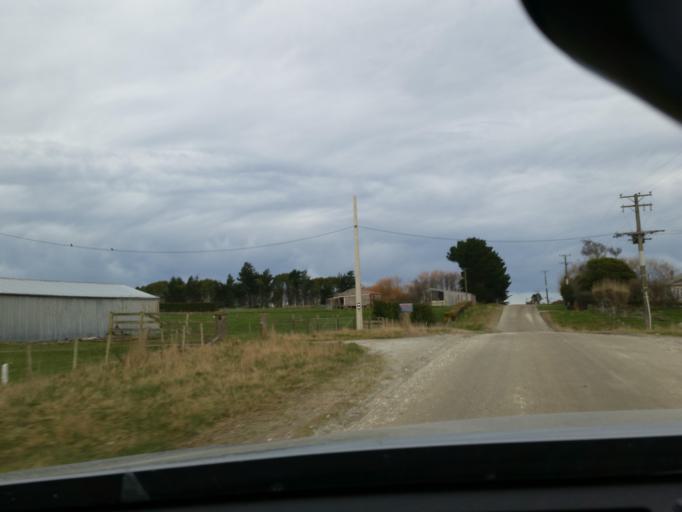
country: NZ
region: Southland
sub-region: Invercargill City
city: Invercargill
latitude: -46.4158
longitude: 168.5061
